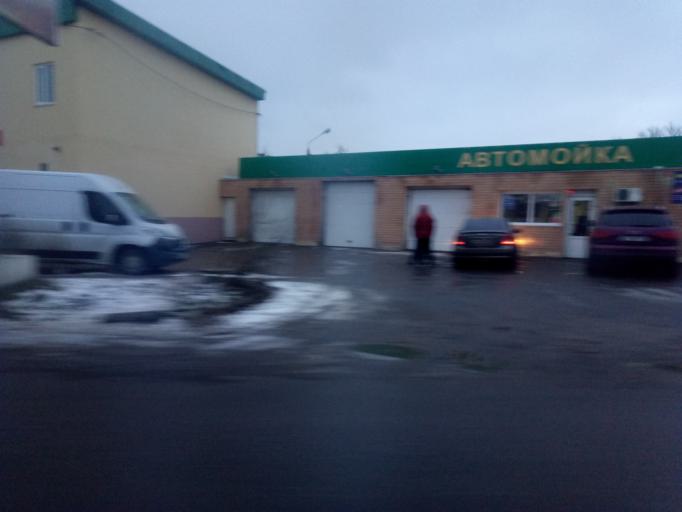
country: RU
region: Tula
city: Tula
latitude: 54.1955
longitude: 37.5763
